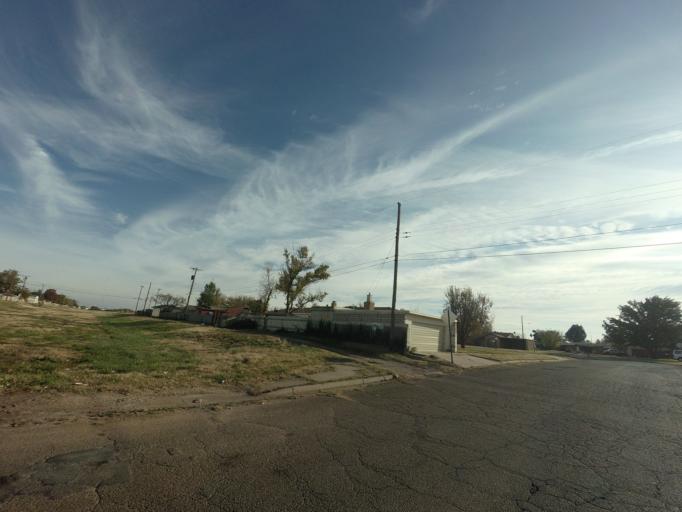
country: US
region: New Mexico
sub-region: Curry County
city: Clovis
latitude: 34.4240
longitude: -103.2241
